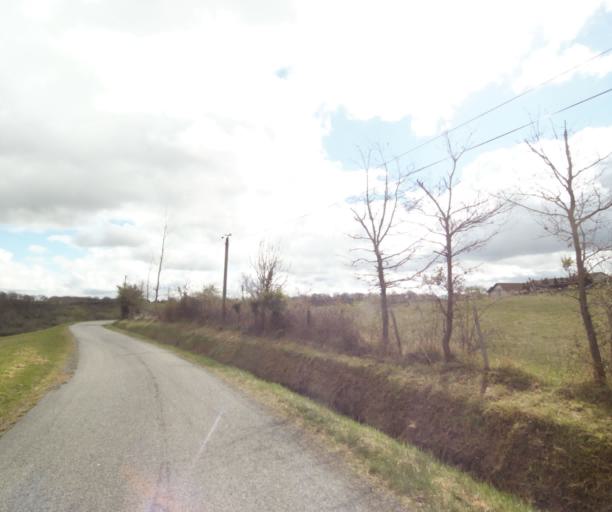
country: FR
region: Midi-Pyrenees
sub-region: Departement de l'Ariege
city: Saverdun
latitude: 43.2052
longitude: 1.5755
